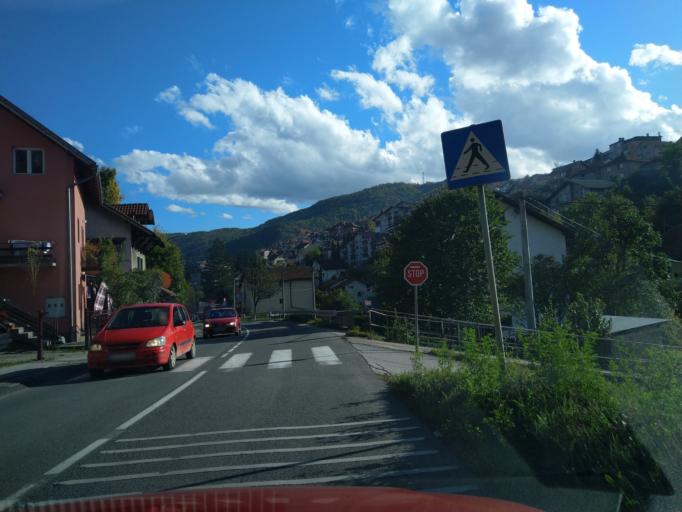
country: RS
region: Central Serbia
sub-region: Zlatiborski Okrug
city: Uzice
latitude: 43.8607
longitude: 19.8268
